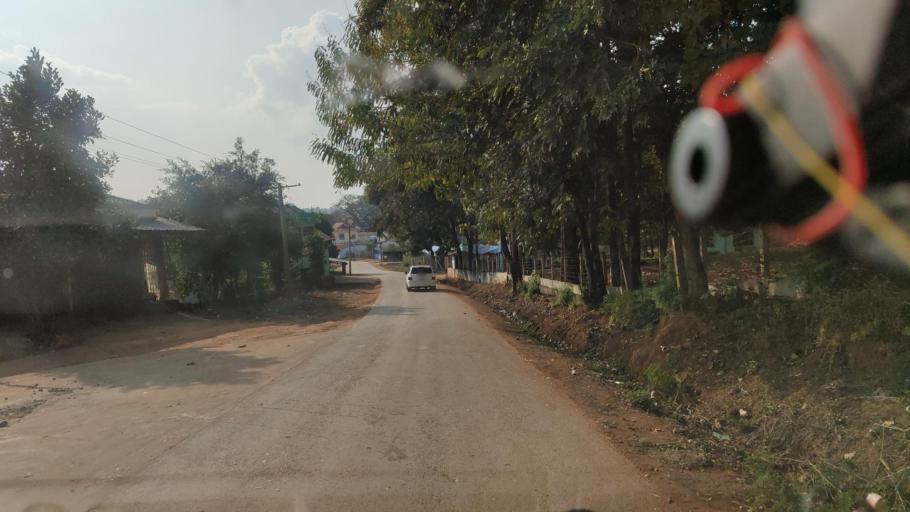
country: CN
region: Yunnan
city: Nayun
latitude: 21.8459
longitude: 99.6913
